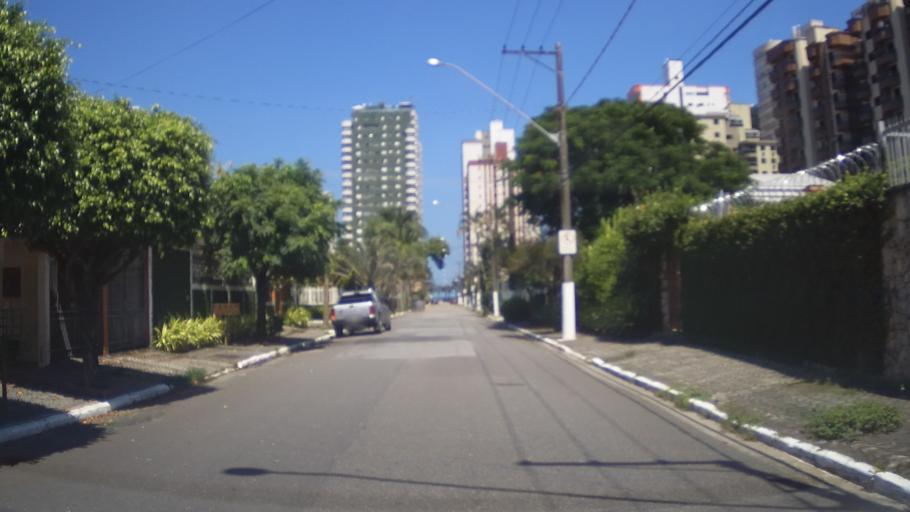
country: BR
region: Sao Paulo
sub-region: Praia Grande
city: Praia Grande
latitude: -24.0117
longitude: -46.4047
